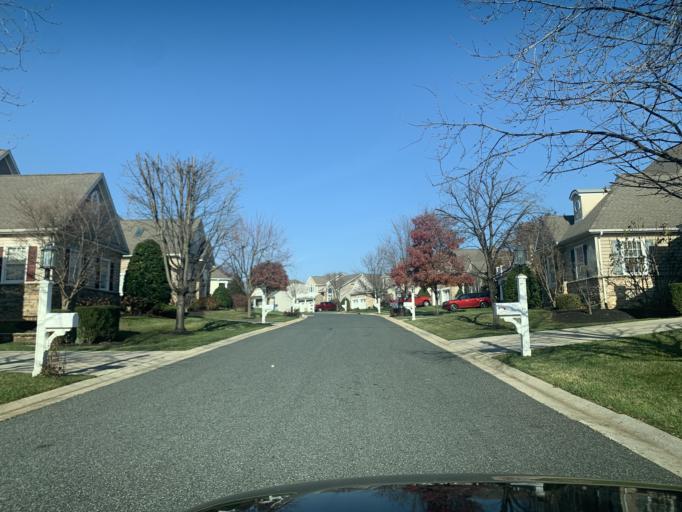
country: US
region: Maryland
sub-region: Harford County
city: Havre de Grace
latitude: 39.5507
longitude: -76.1273
